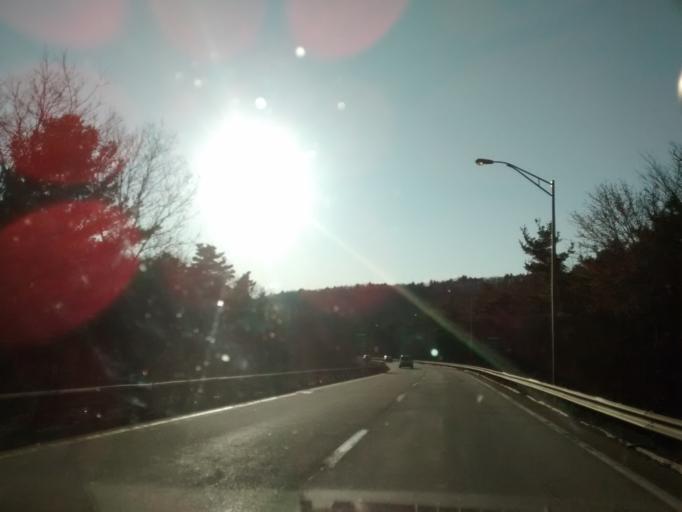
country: US
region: Massachusetts
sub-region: Worcester County
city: Sturbridge
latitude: 42.1314
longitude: -72.0573
